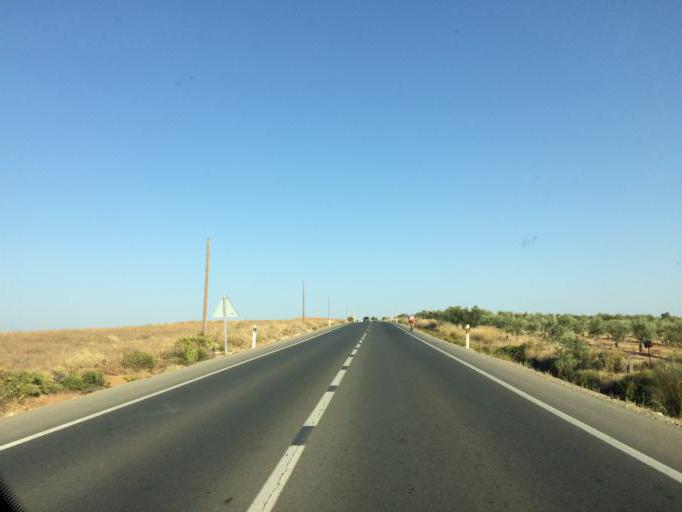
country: ES
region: Andalusia
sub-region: Provincia de Malaga
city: Campillos
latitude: 37.0520
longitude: -4.7762
